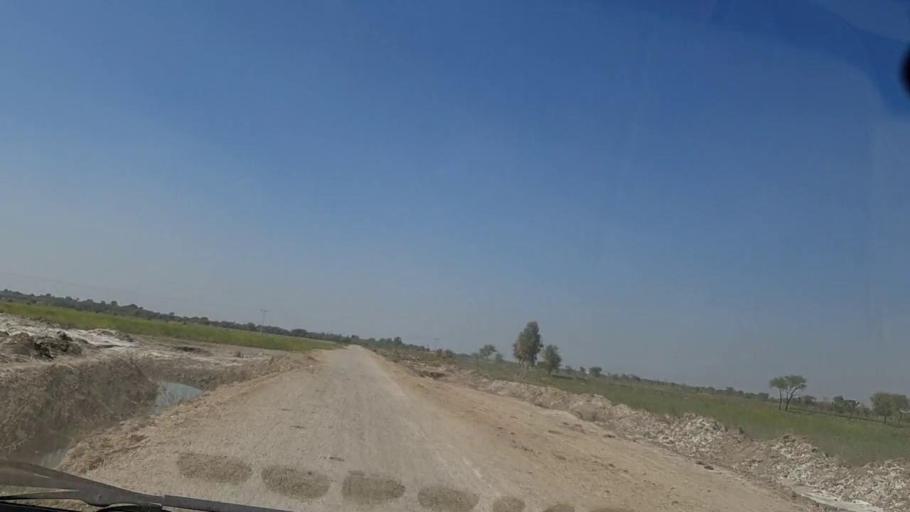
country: PK
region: Sindh
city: Mirwah Gorchani
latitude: 25.3777
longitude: 68.9792
